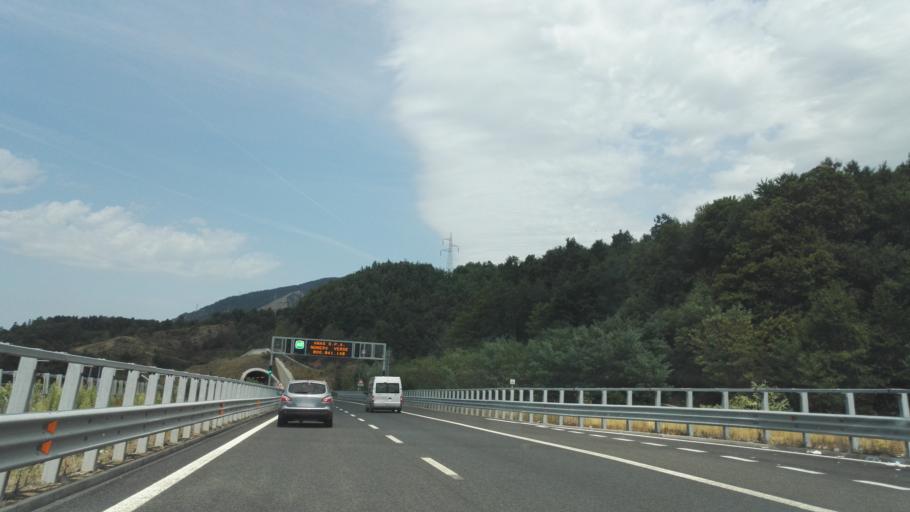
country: IT
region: Basilicate
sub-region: Provincia di Potenza
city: Lagonegro
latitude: 40.1068
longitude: 15.7948
